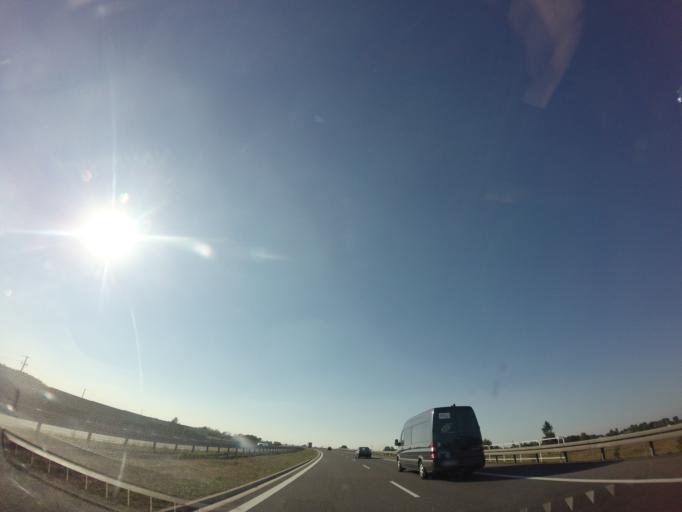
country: PL
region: Lubusz
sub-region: Powiat gorzowski
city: Deszczno
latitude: 52.6553
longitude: 15.3375
